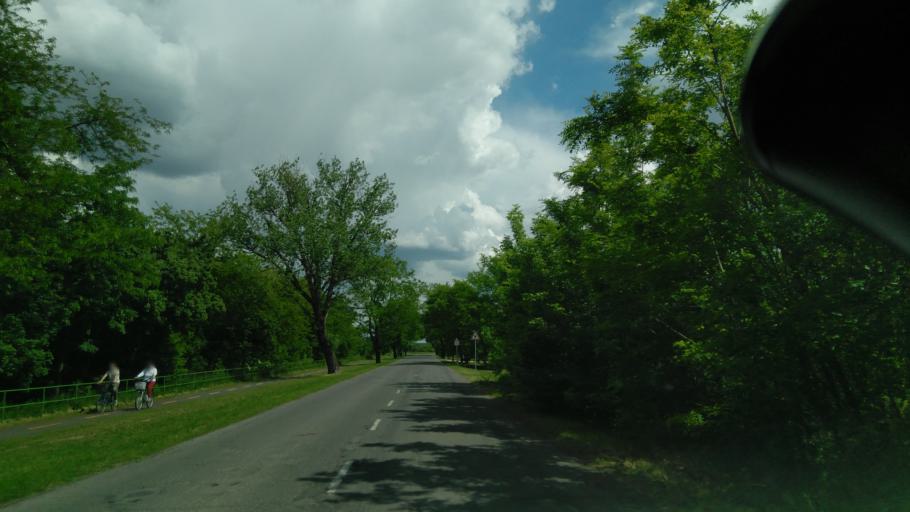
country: HU
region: Bekes
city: Korosladany
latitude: 46.9705
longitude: 21.0656
